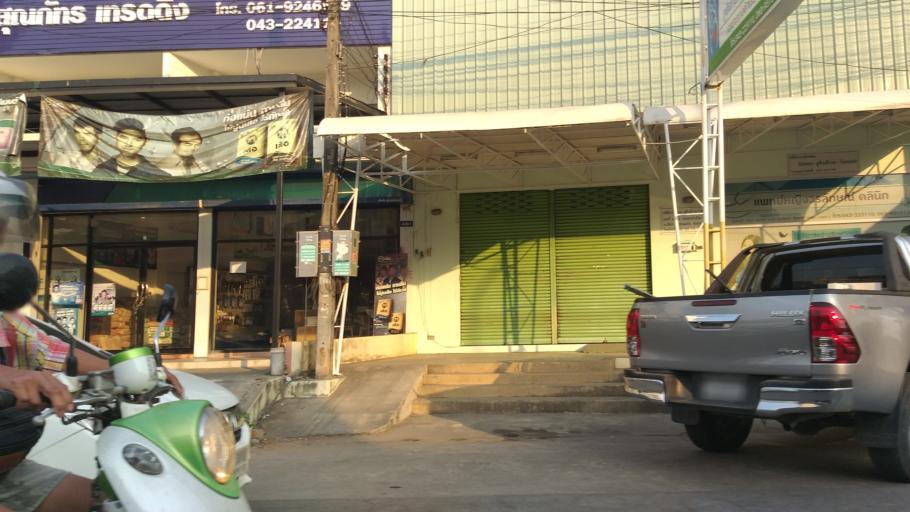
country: TH
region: Khon Kaen
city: Khon Kaen
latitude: 16.4229
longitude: 102.8332
